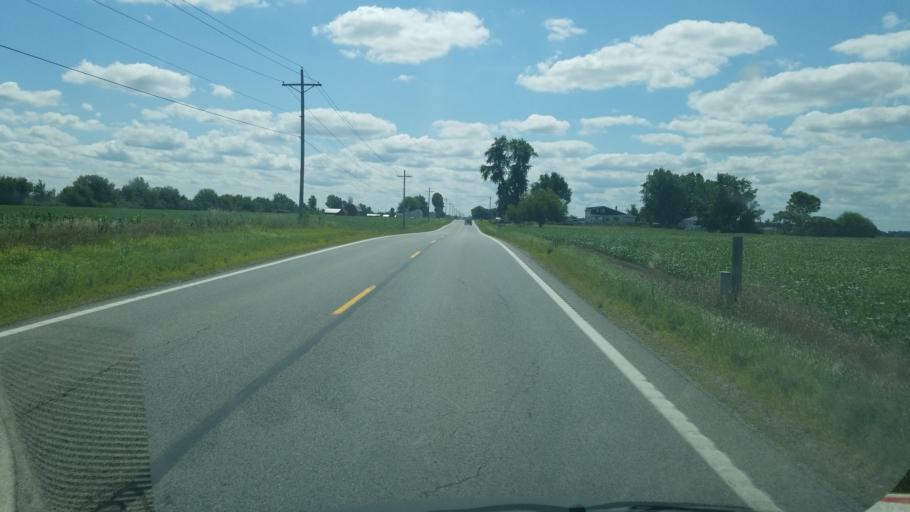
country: US
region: Ohio
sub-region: Fulton County
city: Delta
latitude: 41.6385
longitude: -84.0349
